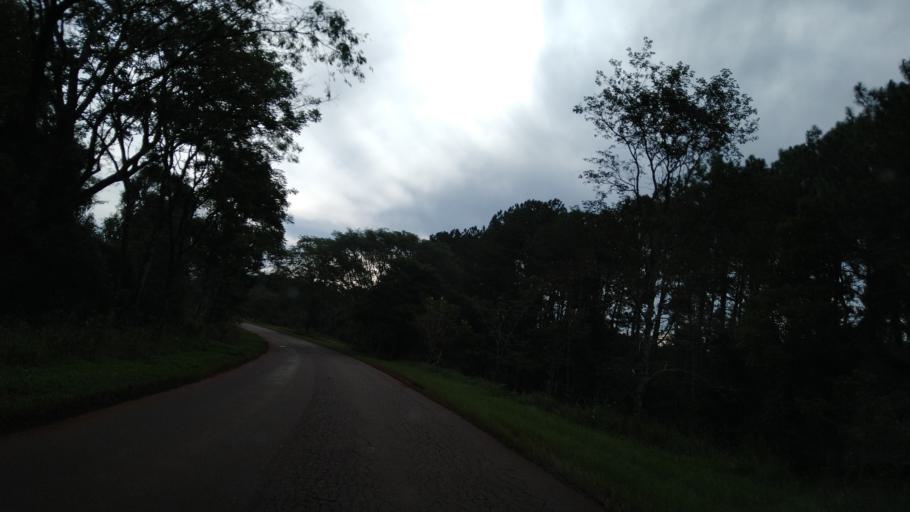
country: AR
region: Misiones
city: Capiovi
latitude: -26.9343
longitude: -55.0849
